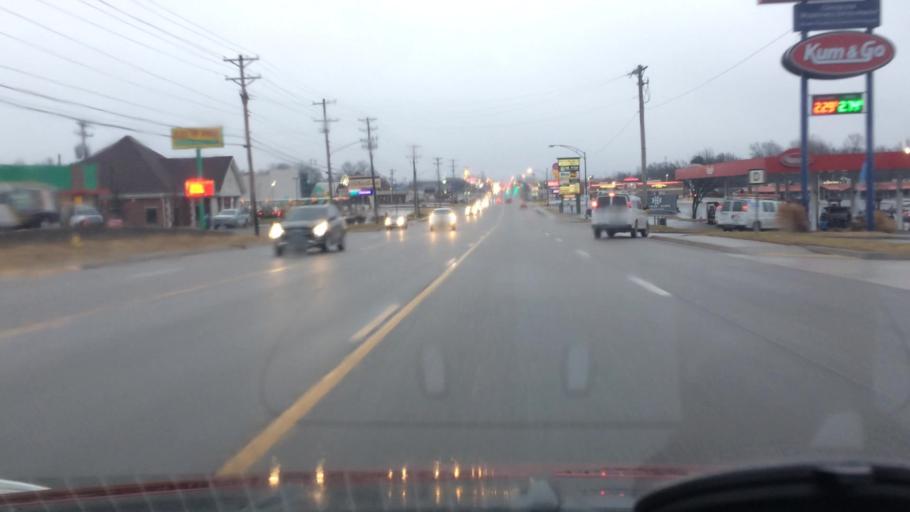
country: US
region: Missouri
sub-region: Greene County
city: Springfield
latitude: 37.1806
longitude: -93.2380
